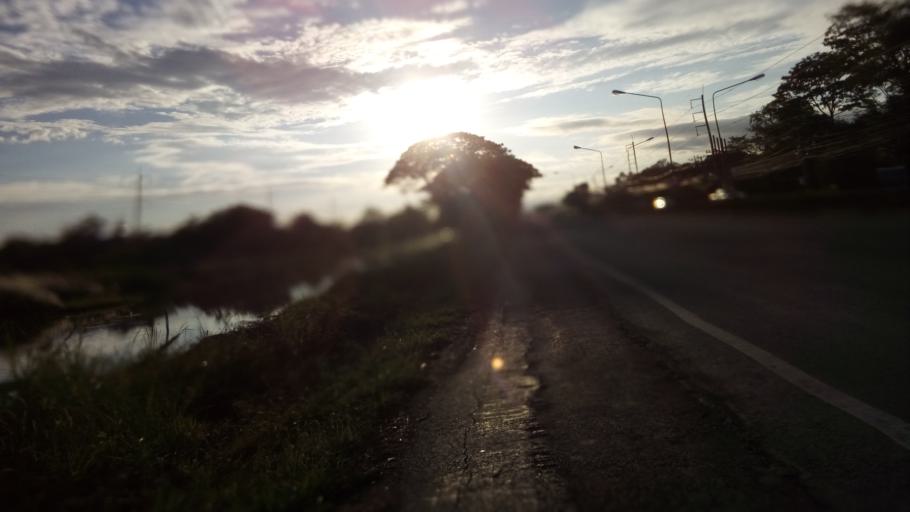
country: TH
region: Nakhon Nayok
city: Ongkharak
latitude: 14.0867
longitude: 100.9220
